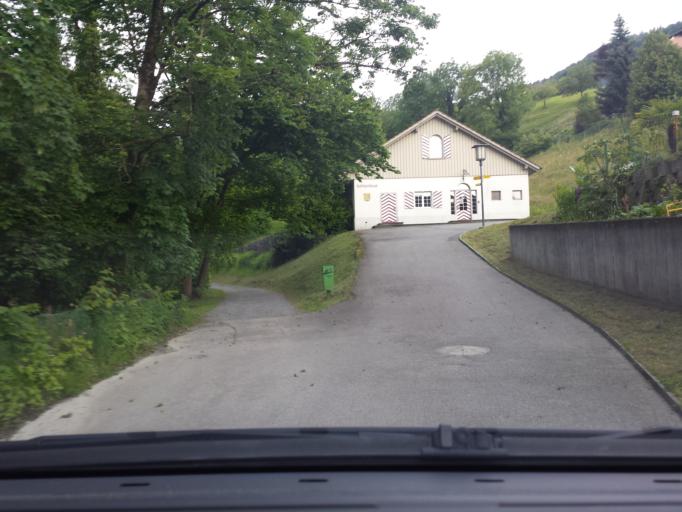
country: CH
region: Appenzell Innerrhoden
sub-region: Appenzell Inner Rhodes
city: Balgach
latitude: 47.4237
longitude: 9.6046
